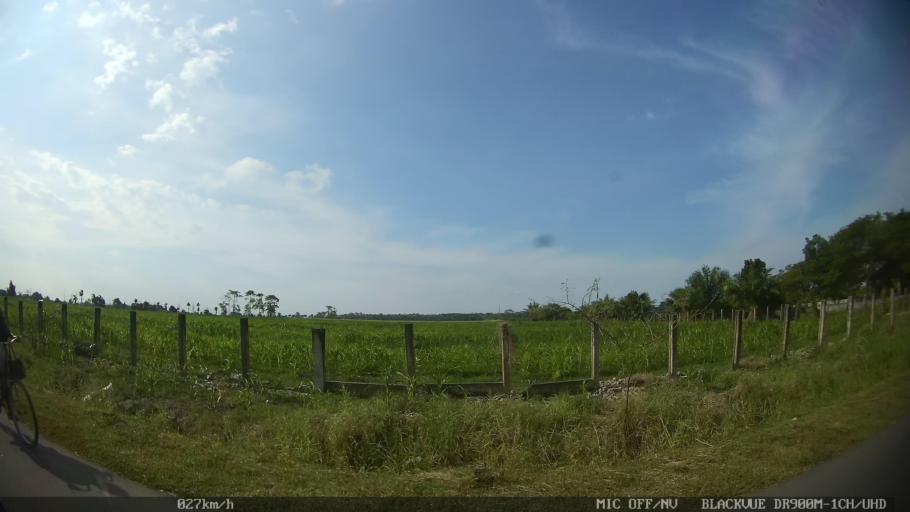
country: ID
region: North Sumatra
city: Percut
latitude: 3.5932
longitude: 98.7974
